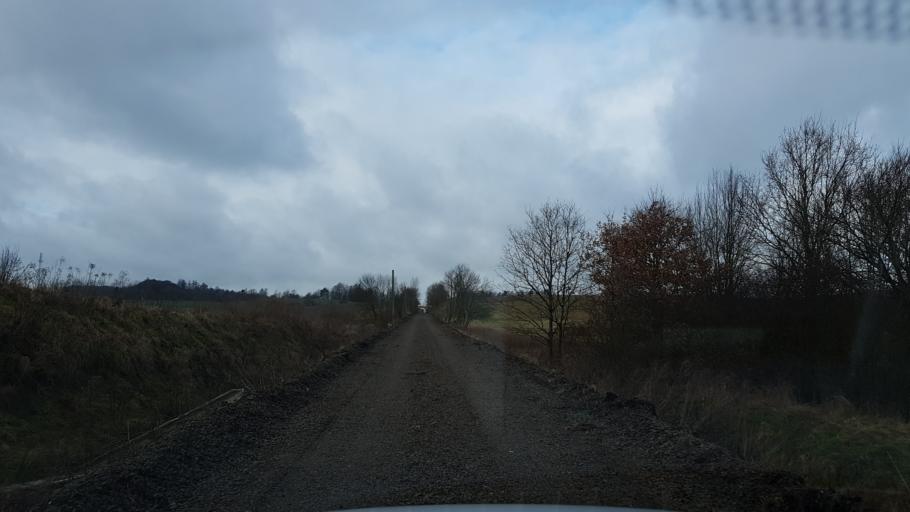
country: PL
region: West Pomeranian Voivodeship
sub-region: Powiat swidwinski
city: Polczyn-Zdroj
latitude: 53.7841
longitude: 16.0592
